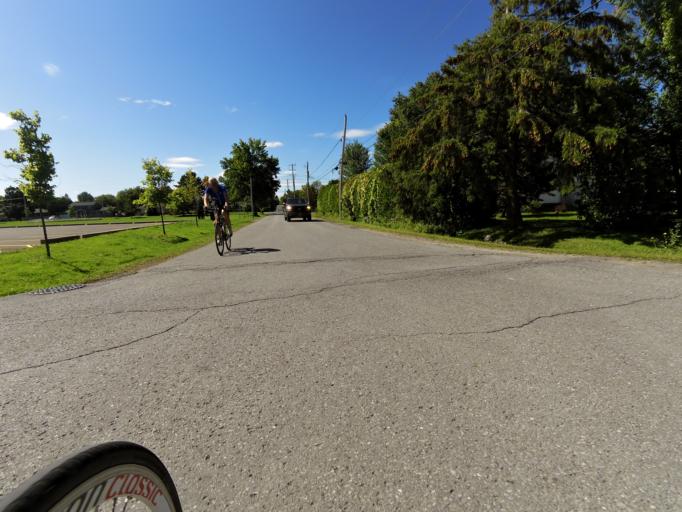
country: CA
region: Ontario
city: Bells Corners
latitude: 45.1882
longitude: -75.8289
